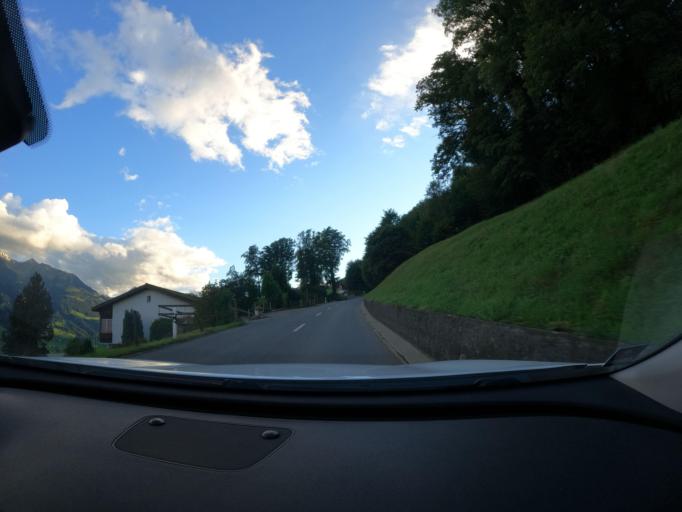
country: CH
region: Obwalden
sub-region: Obwalden
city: Sachseln
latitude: 46.8910
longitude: 8.2234
